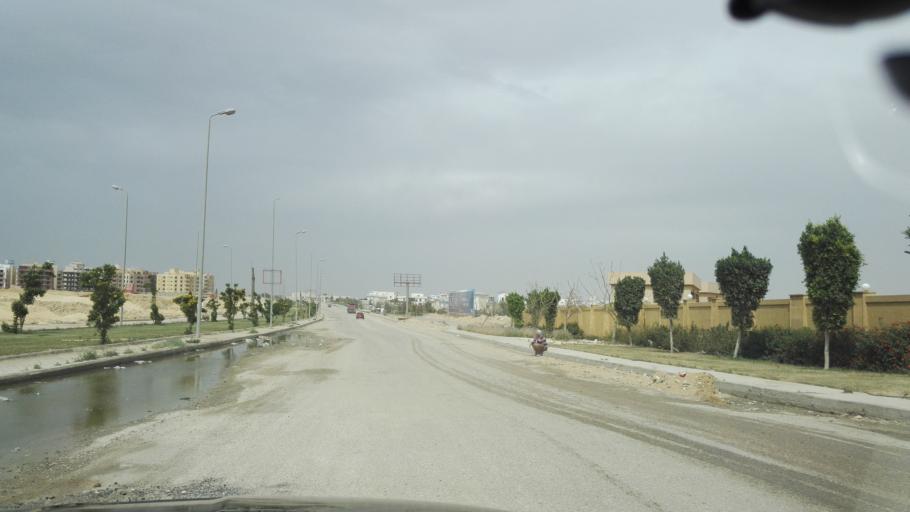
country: EG
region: Muhafazat al Qalyubiyah
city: Al Khankah
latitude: 30.0285
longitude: 31.5293
